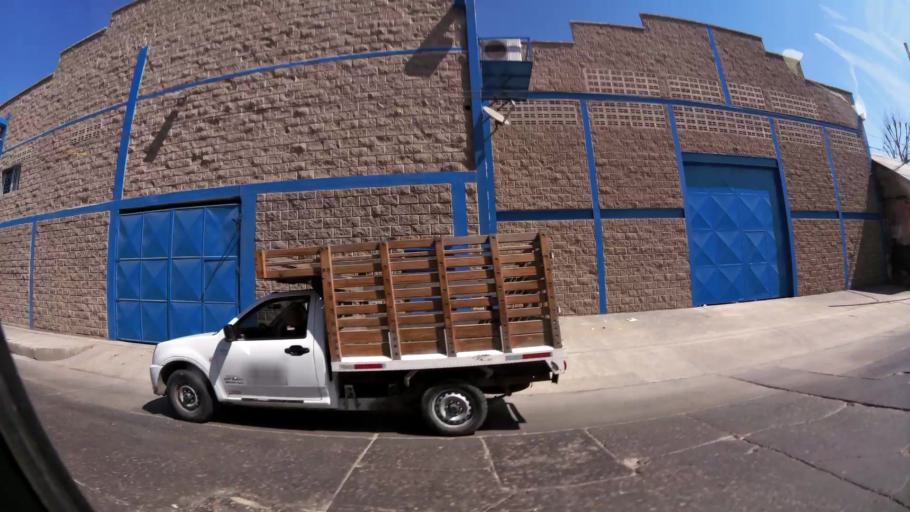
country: CO
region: Atlantico
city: Barranquilla
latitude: 10.9742
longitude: -74.7829
